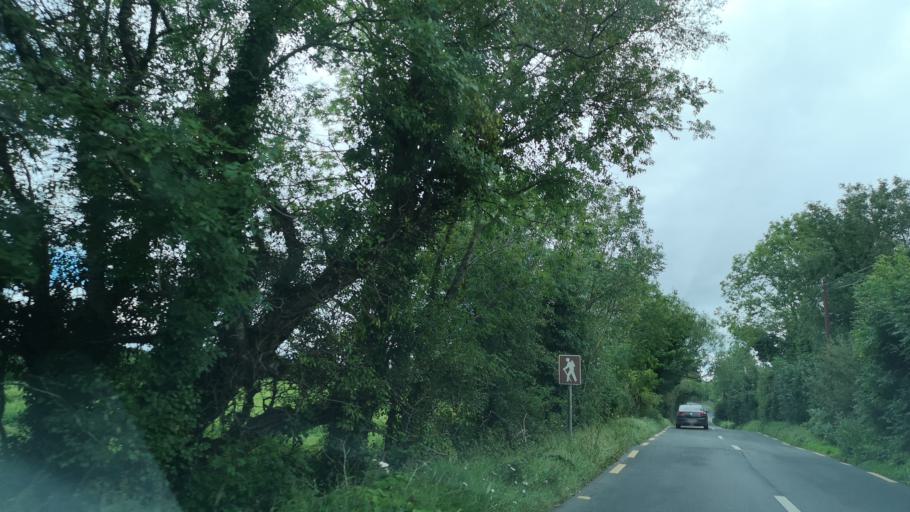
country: IE
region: Leinster
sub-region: Uibh Fhaili
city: Banagher
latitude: 53.2800
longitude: -8.0641
